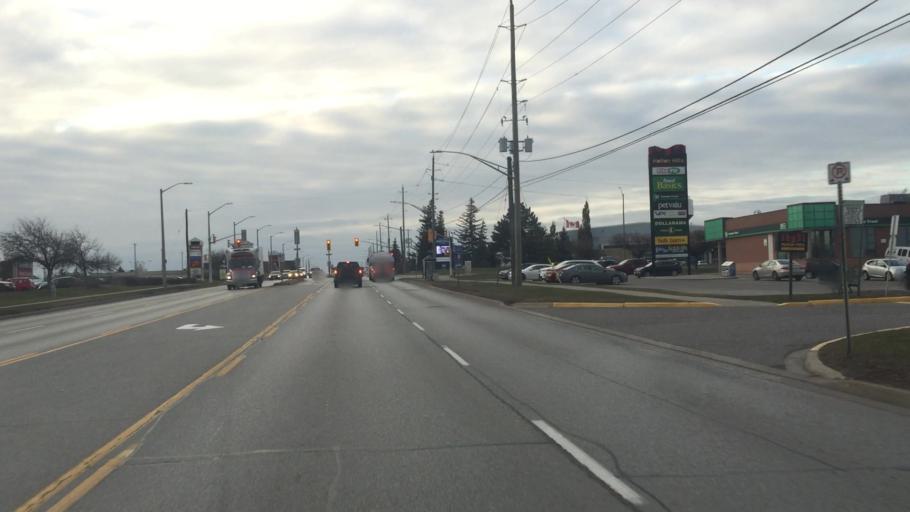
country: CA
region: Ontario
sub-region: Halton
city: Milton
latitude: 43.6499
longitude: -79.8965
